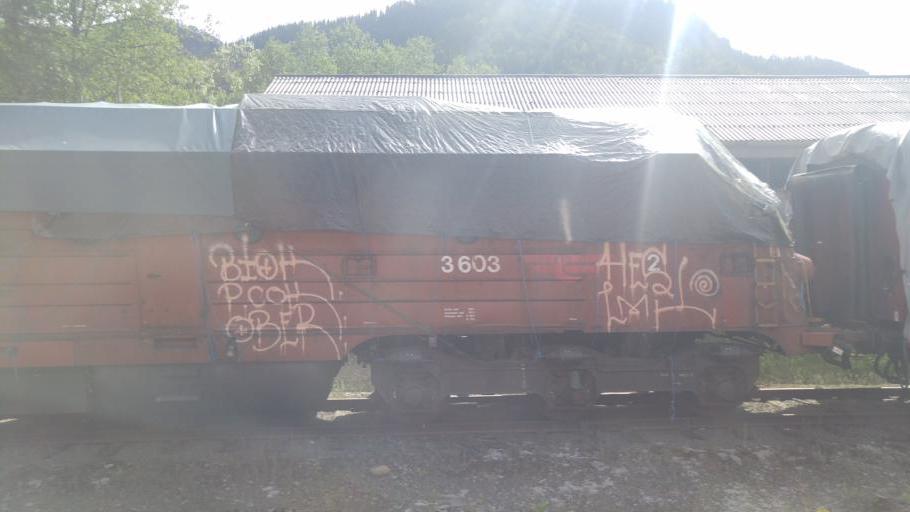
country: NO
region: Sor-Trondelag
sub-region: Midtre Gauldal
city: Storen
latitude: 63.0579
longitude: 10.2874
